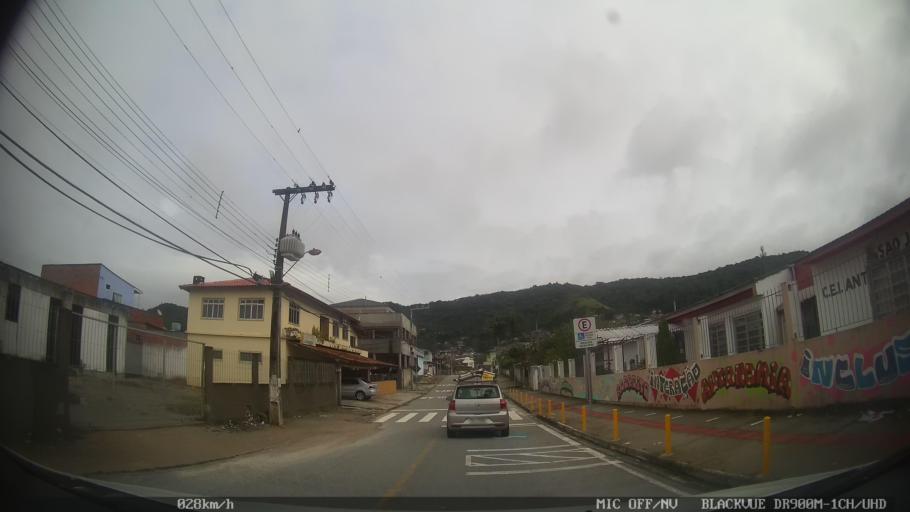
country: BR
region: Santa Catarina
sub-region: Biguacu
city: Biguacu
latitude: -27.5412
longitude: -48.6452
